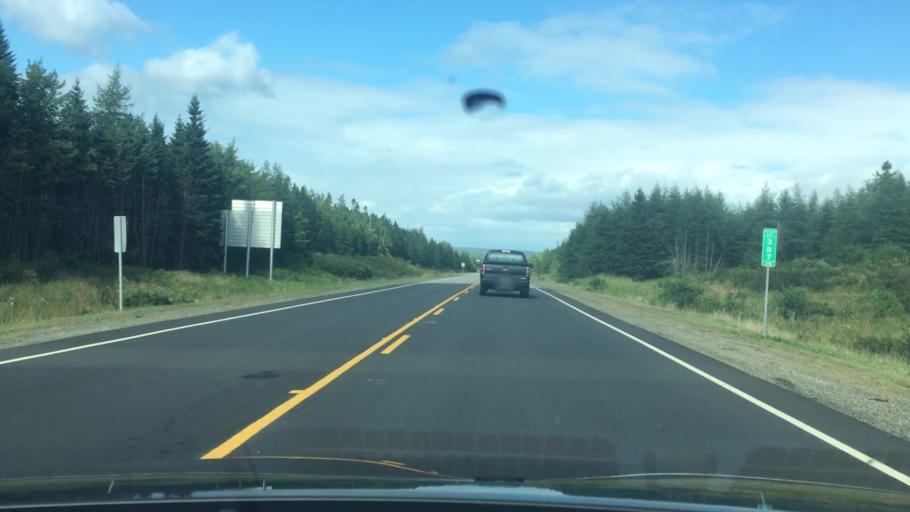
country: CA
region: Nova Scotia
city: Princeville
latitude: 45.6192
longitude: -61.0514
